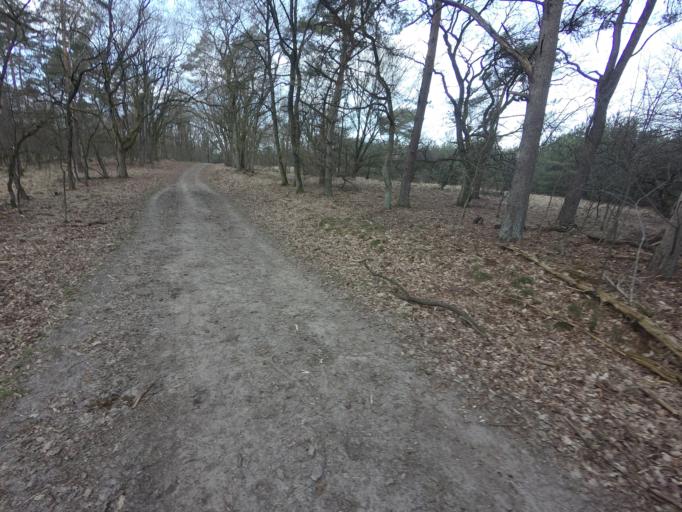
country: NL
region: Limburg
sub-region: Gemeente Roerdalen
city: Vlodrop
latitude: 51.1609
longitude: 6.1204
